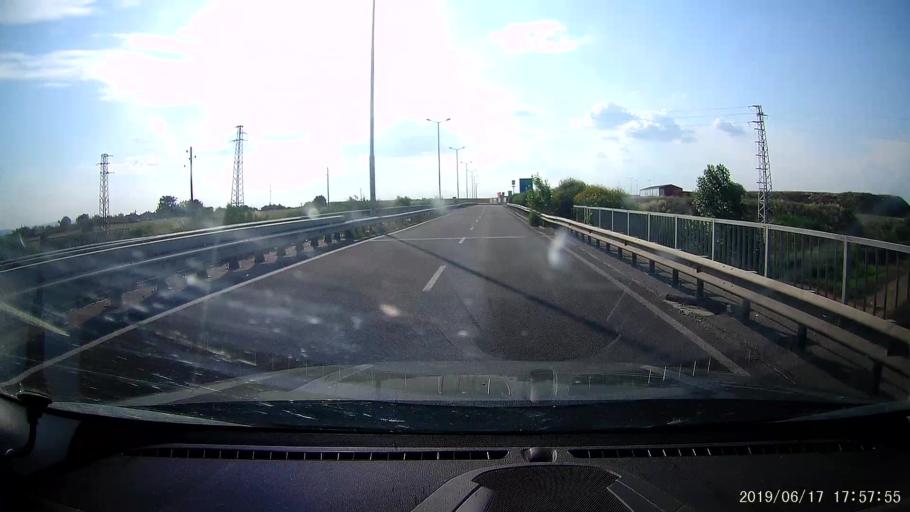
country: BG
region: Khaskovo
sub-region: Obshtina Svilengrad
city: Svilengrad
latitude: 41.7236
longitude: 26.3286
